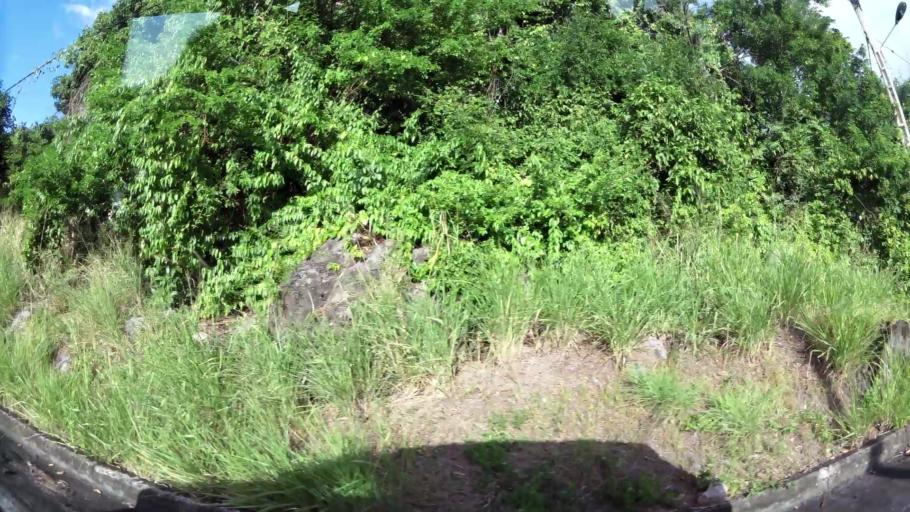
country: GP
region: Guadeloupe
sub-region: Guadeloupe
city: Pointe-Noire
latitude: 16.1882
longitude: -61.7806
